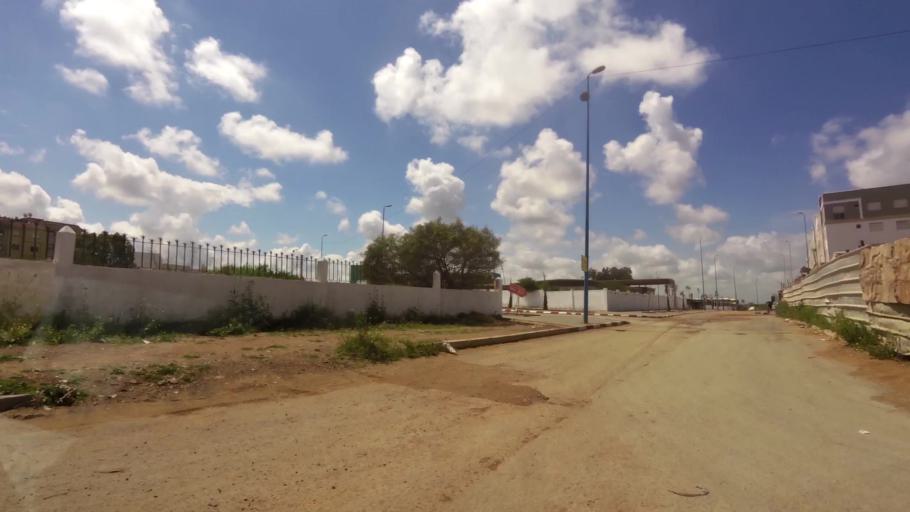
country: MA
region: Grand Casablanca
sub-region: Nouaceur
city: Dar Bouazza
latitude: 33.5294
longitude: -7.7401
